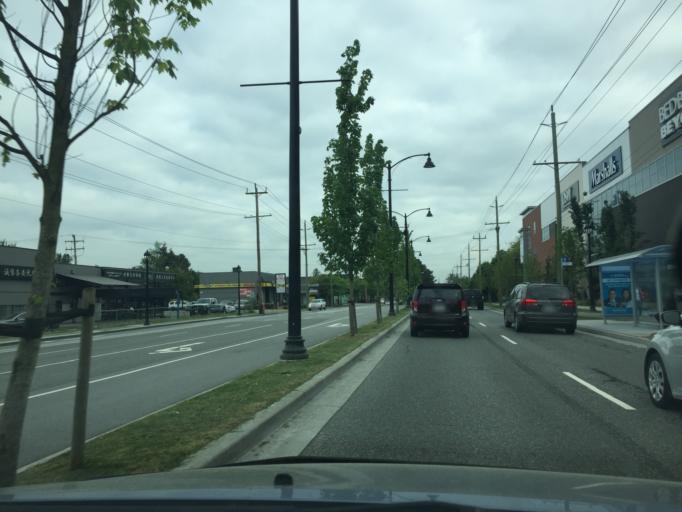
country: CA
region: British Columbia
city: Richmond
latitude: 49.1762
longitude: -123.1245
